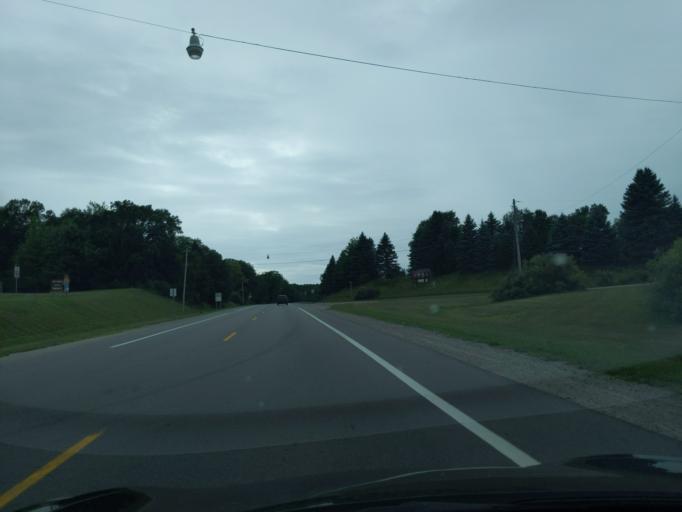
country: US
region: Michigan
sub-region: Clare County
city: Harrison
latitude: 44.0193
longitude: -84.8119
